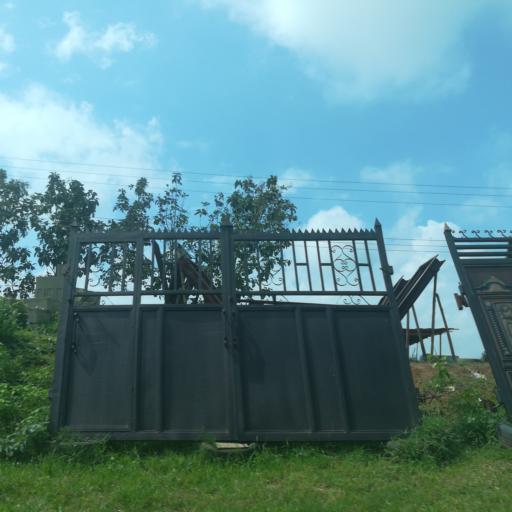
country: NG
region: Lagos
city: Ikorodu
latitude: 6.6712
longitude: 3.6681
